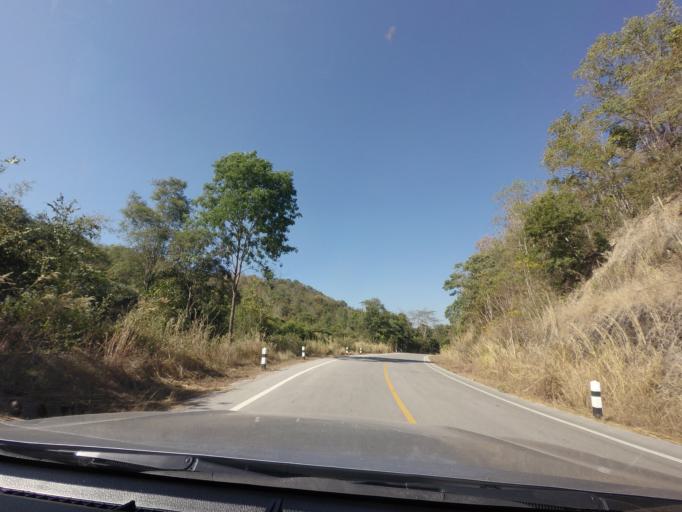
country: TH
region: Lampang
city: Chae Hom
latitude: 18.5782
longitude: 99.6270
